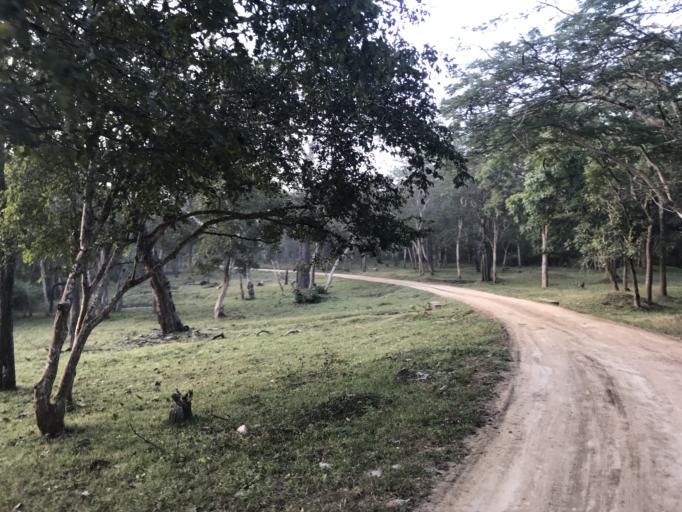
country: IN
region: Karnataka
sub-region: Mysore
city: Heggadadevankote
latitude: 12.0063
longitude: 76.2235
